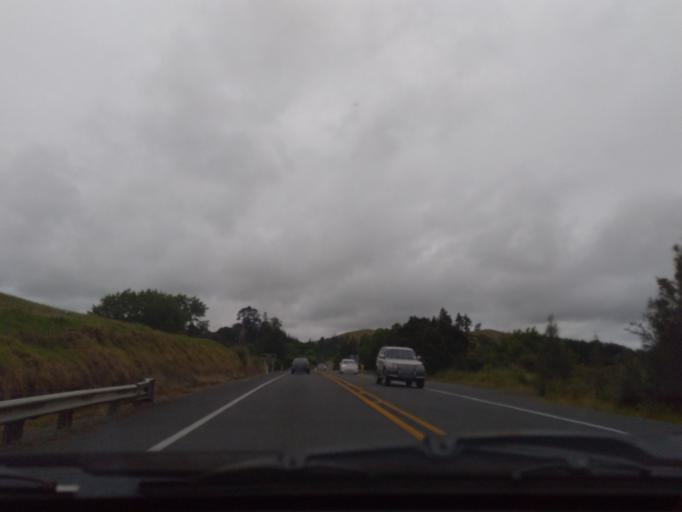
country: NZ
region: Northland
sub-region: Whangarei
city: Whangarei
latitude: -35.8315
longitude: 174.3145
